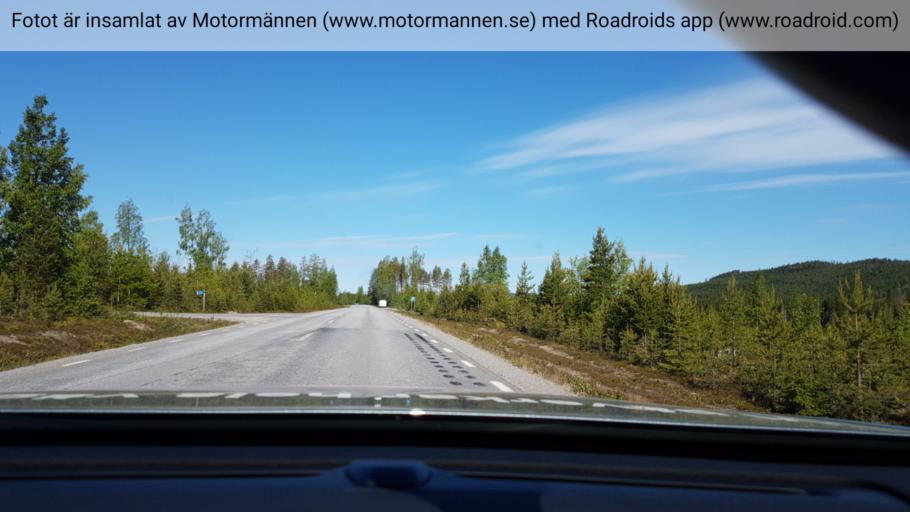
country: SE
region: Vaesterbotten
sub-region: Bjurholms Kommun
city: Bjurholm
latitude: 63.9526
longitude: 18.8879
